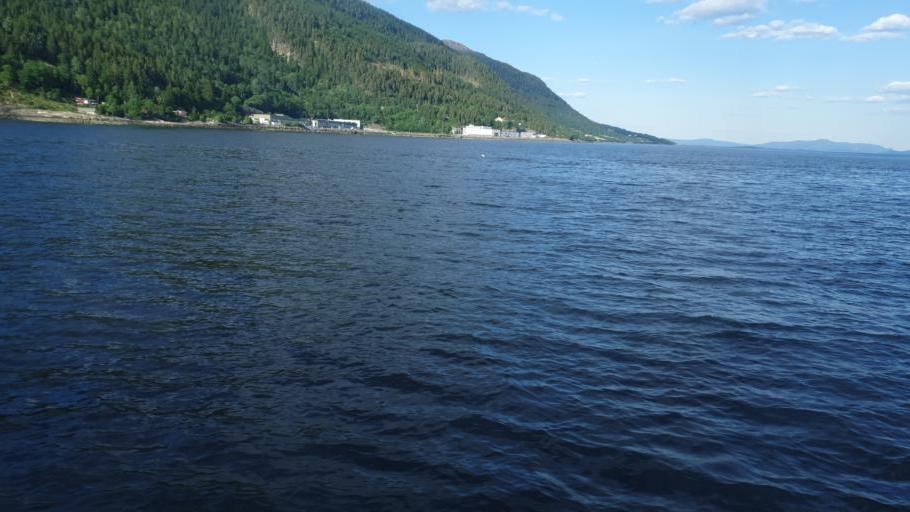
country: NO
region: Sor-Trondelag
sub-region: Trondheim
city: Trondheim
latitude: 63.5523
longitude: 10.2266
